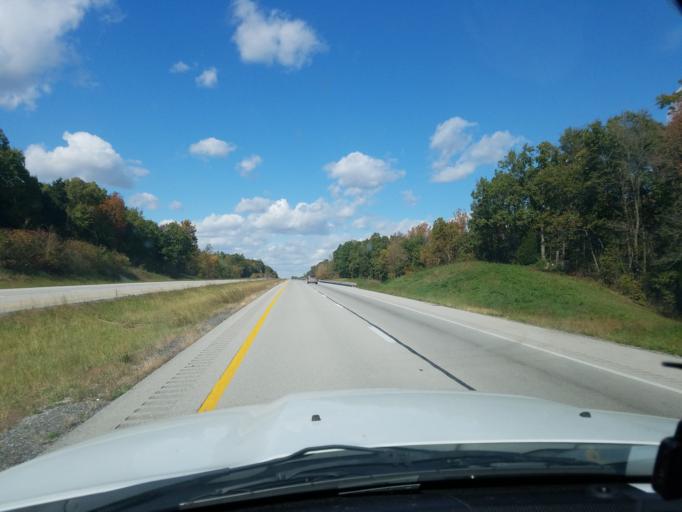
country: US
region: Kentucky
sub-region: Daviess County
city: Masonville
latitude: 37.5789
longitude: -86.9560
